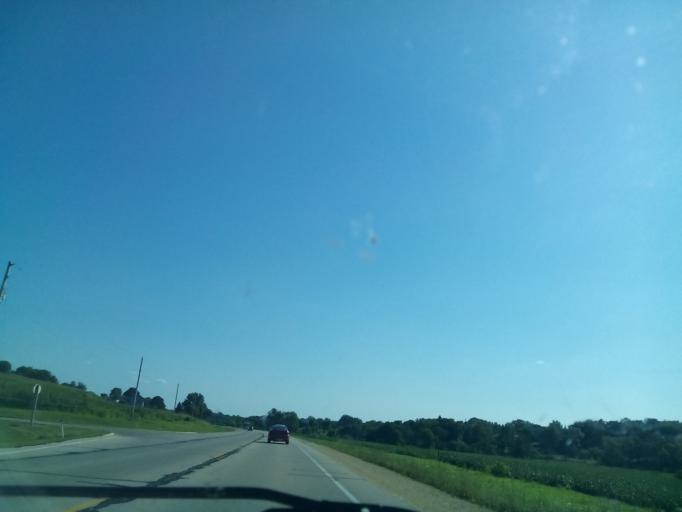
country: US
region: Wisconsin
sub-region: Green County
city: New Glarus
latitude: 42.8404
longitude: -89.6342
